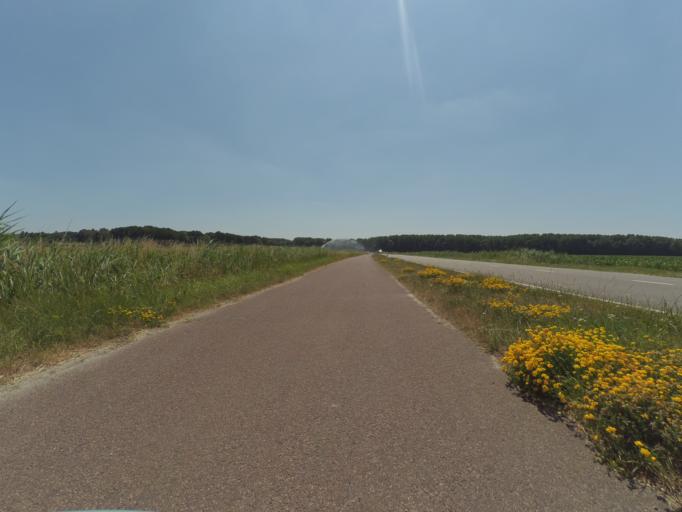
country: NL
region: North Brabant
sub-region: Gemeente Bergen op Zoom
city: Halsteren
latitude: 51.5200
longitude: 4.2628
